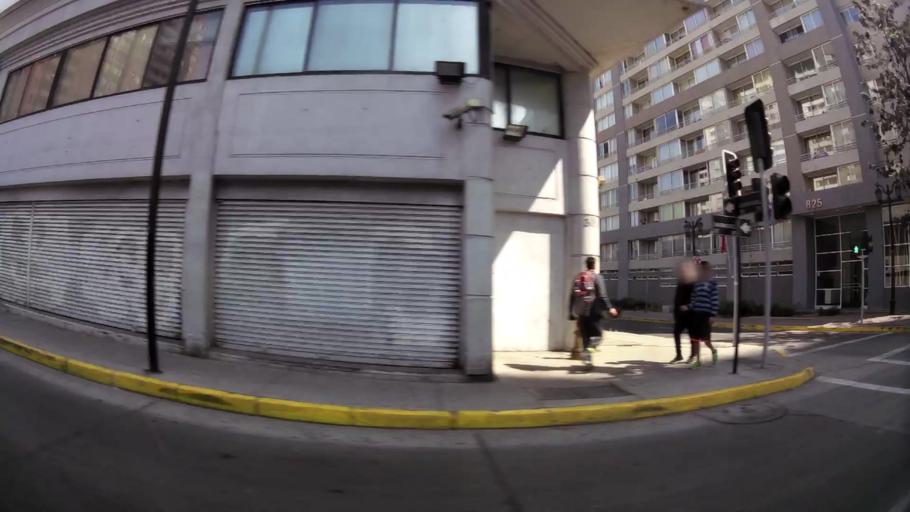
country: CL
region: Santiago Metropolitan
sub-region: Provincia de Santiago
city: Santiago
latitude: -33.4486
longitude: -70.6470
